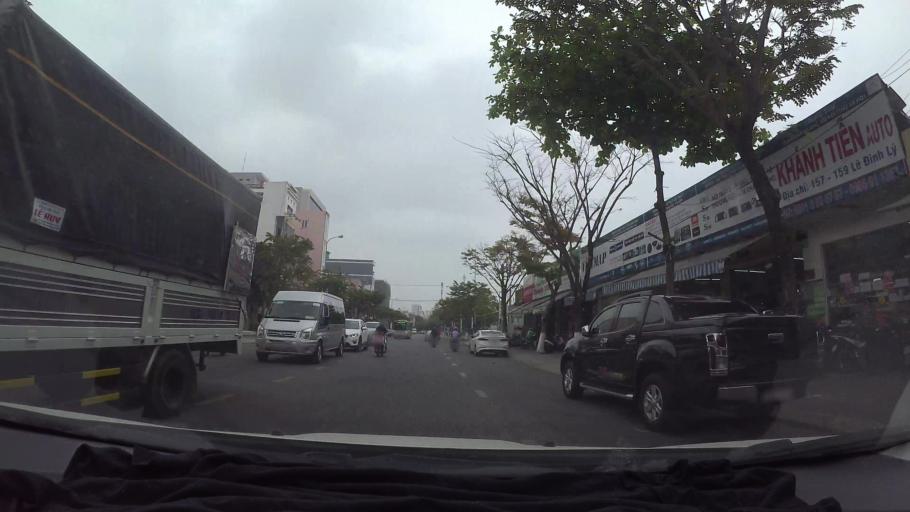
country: VN
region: Da Nang
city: Da Nang
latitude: 16.0528
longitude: 108.2108
